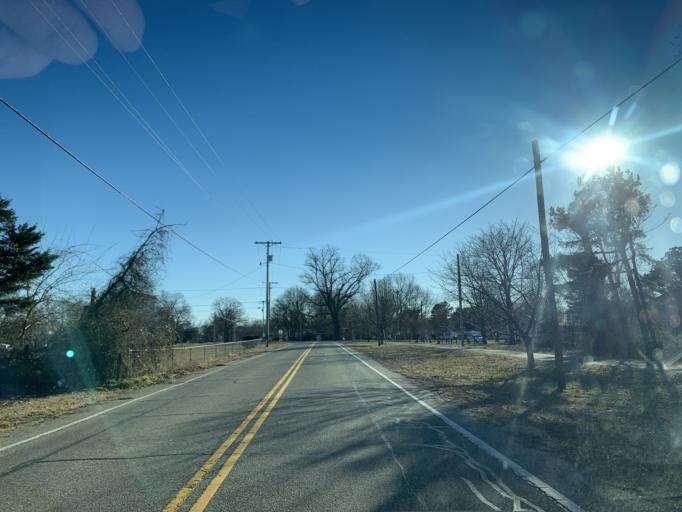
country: US
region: Maryland
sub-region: Saint Mary's County
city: Charlotte Hall
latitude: 38.5012
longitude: -76.7767
